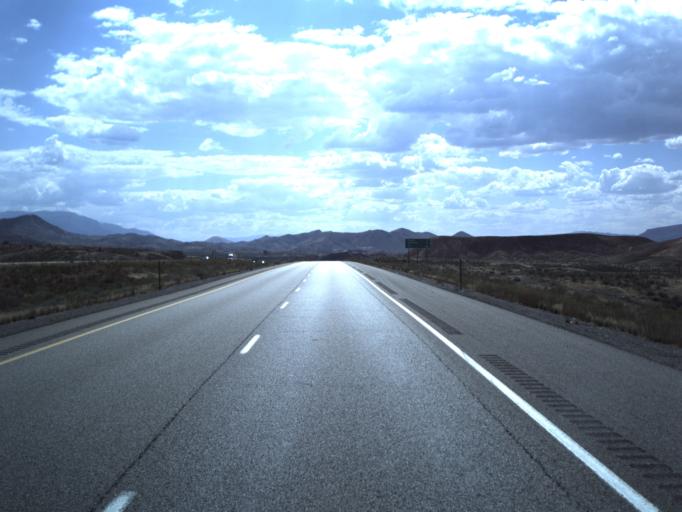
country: US
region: Utah
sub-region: Sevier County
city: Salina
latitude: 38.9274
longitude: -111.8709
